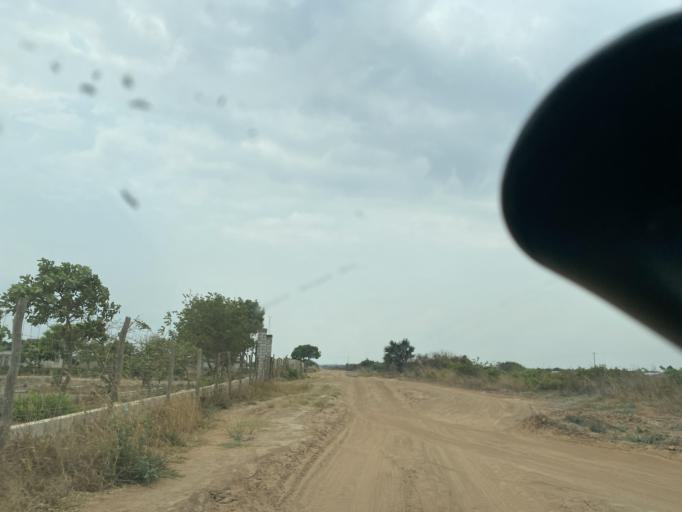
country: ZM
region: Lusaka
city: Lusaka
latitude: -15.2158
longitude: 28.3383
